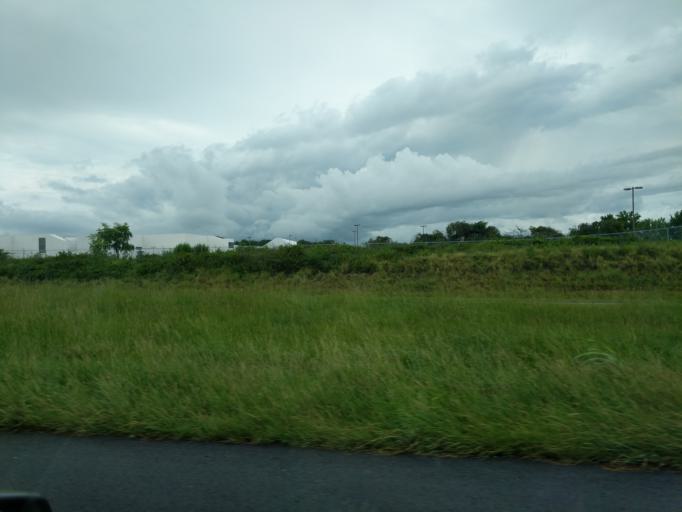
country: US
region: South Carolina
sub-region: Greenville County
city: Greer
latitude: 34.8868
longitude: -82.1875
